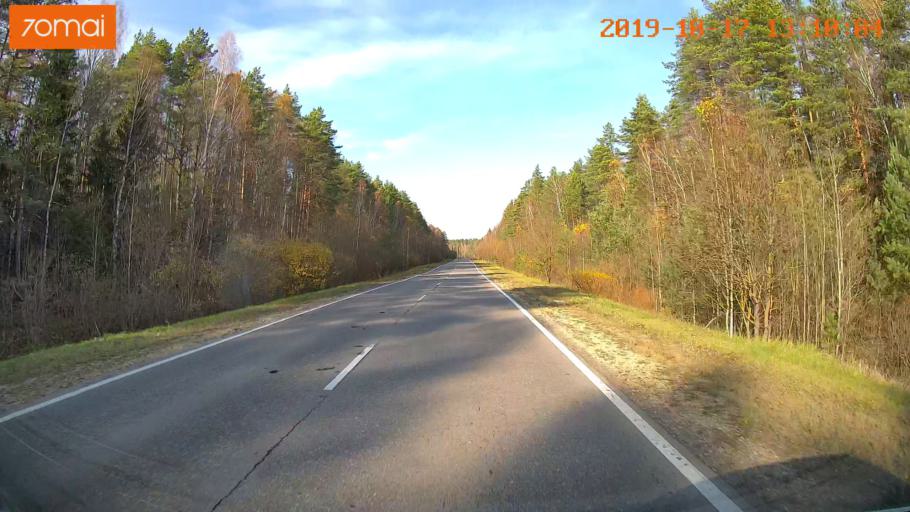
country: RU
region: Rjazan
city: Syntul
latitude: 55.0133
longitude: 41.2590
